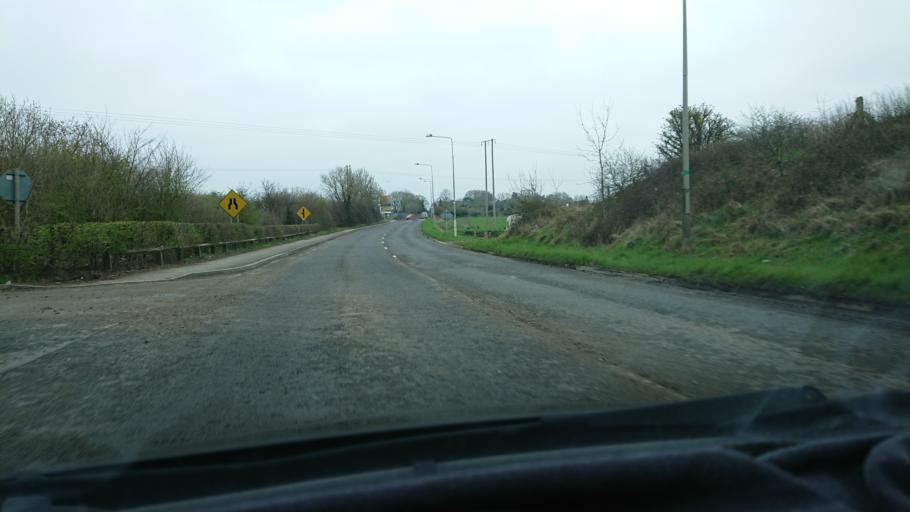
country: IE
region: Leinster
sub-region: Lu
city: Drogheda
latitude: 53.6959
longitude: -6.3676
